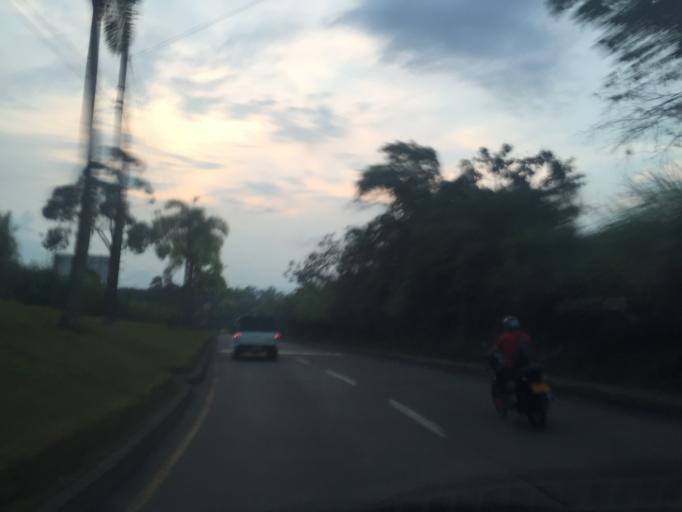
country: CO
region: Risaralda
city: Pereira
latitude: 4.8006
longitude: -75.7534
